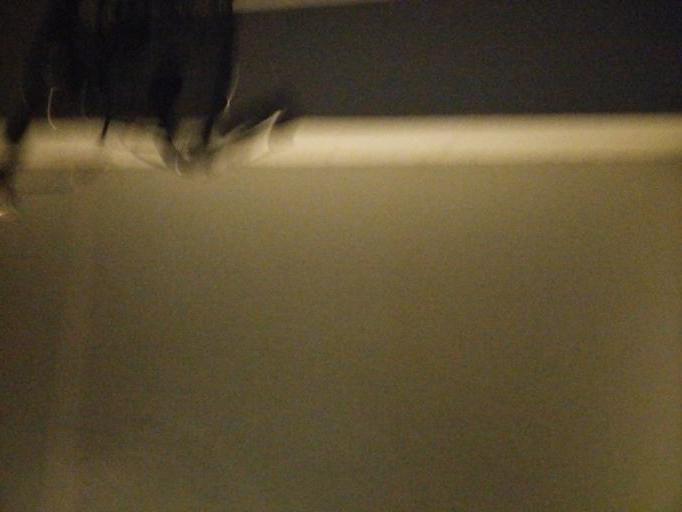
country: TH
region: Pathum Thani
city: Khlong Luang
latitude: 14.0824
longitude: 100.6133
